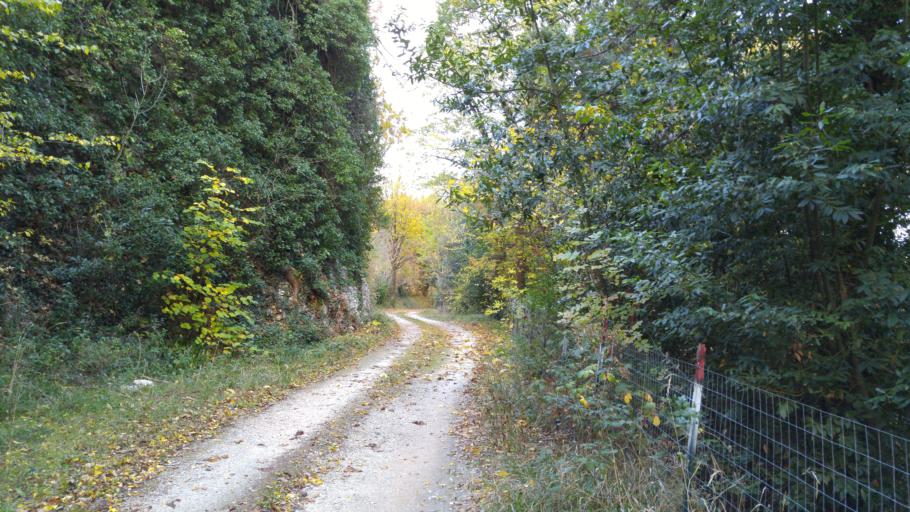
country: IT
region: The Marches
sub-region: Provincia di Pesaro e Urbino
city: Pergola
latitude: 43.5626
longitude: 12.8341
